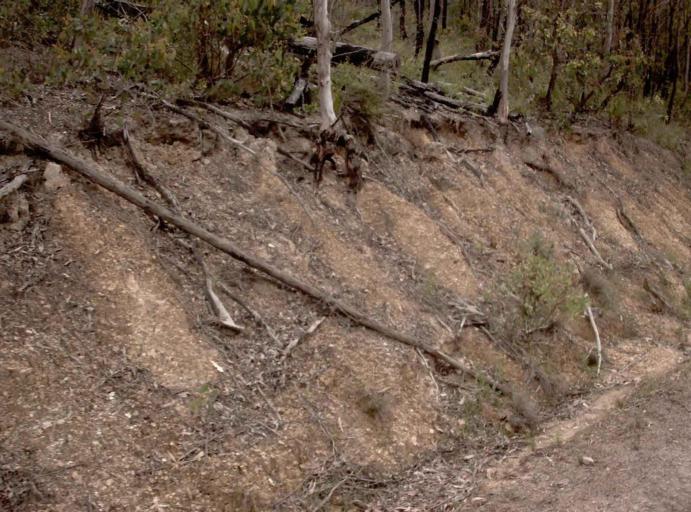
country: AU
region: Victoria
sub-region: East Gippsland
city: Bairnsdale
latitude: -37.6487
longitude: 147.2775
